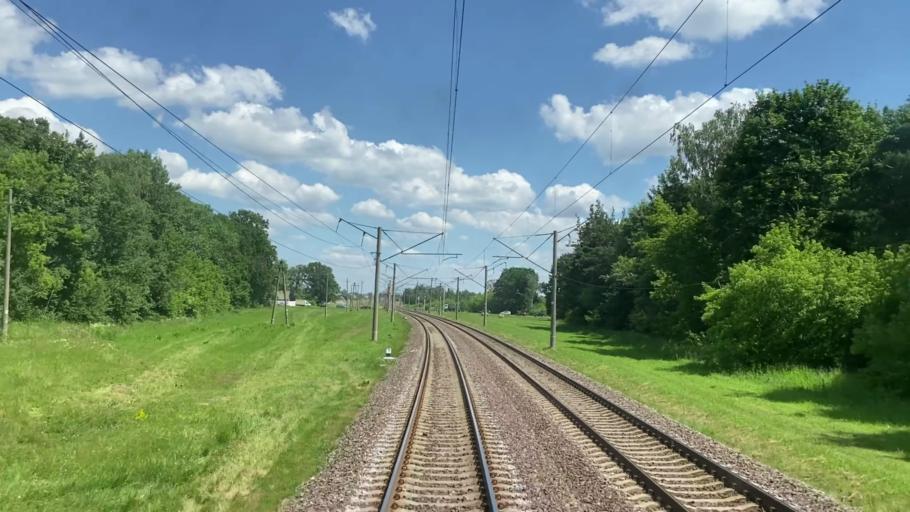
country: BY
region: Brest
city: Ivatsevichy
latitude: 52.6963
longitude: 25.3151
